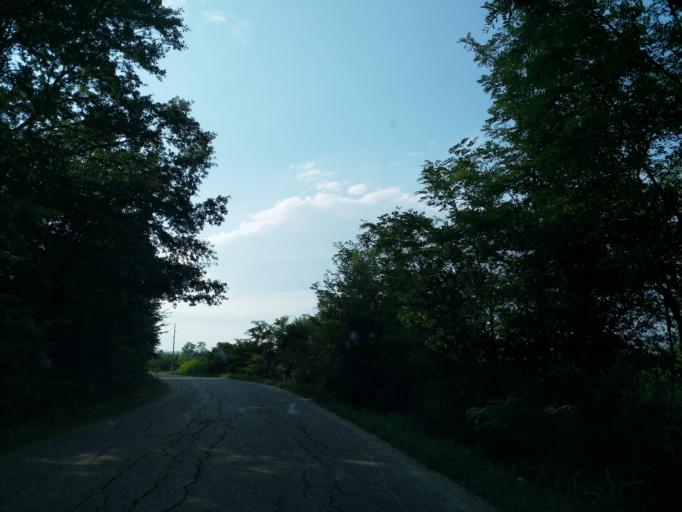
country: RS
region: Central Serbia
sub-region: Pomoravski Okrug
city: Jagodina
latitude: 43.9879
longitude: 21.2125
